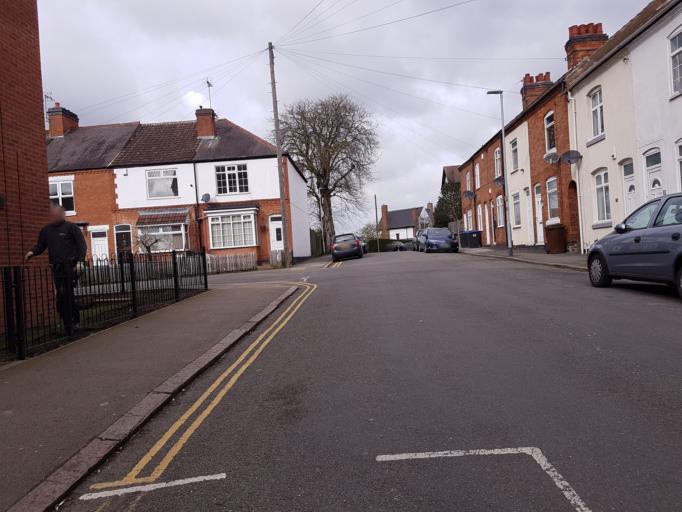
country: GB
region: England
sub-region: Leicestershire
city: Hinckley
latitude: 52.5424
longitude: -1.3762
